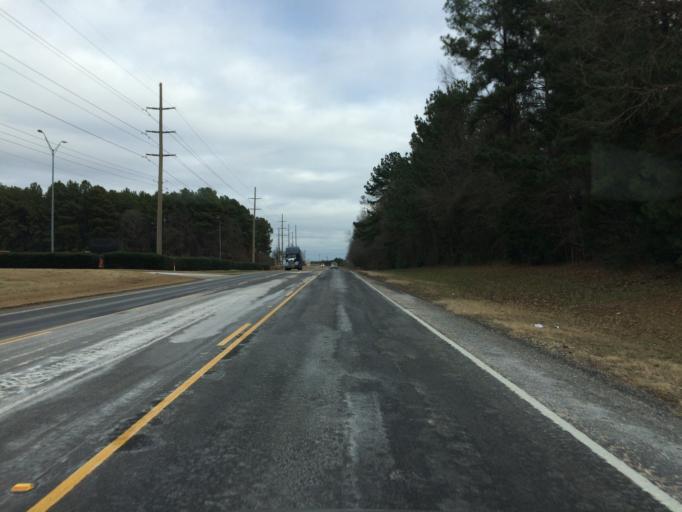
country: US
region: Texas
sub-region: Wood County
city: Mineola
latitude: 32.6881
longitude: -95.4783
